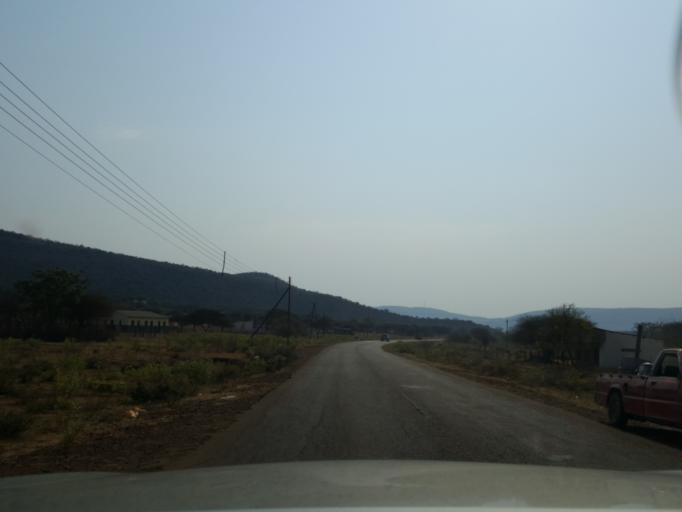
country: BW
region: South East
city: Lobatse
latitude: -25.3068
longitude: 25.8154
